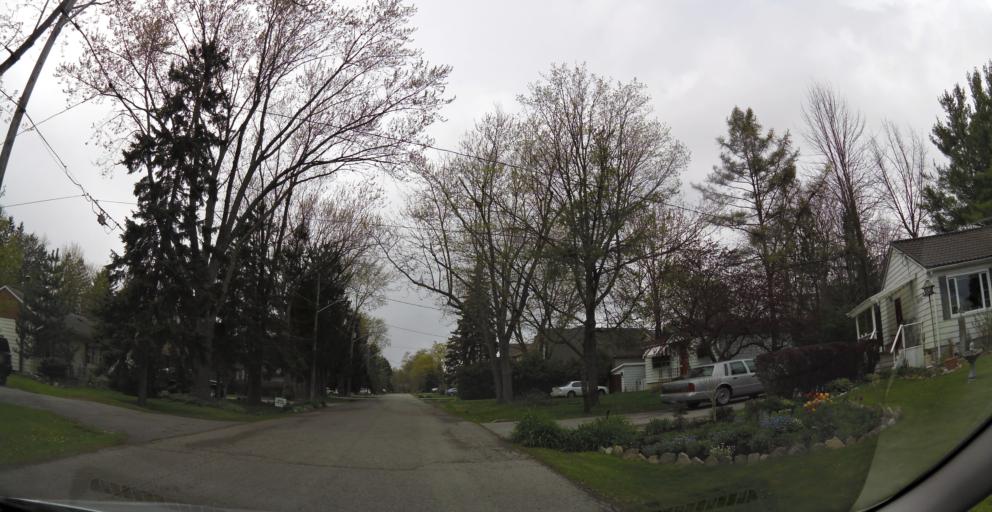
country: CA
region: Ontario
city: Mississauga
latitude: 43.5660
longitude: -79.5802
